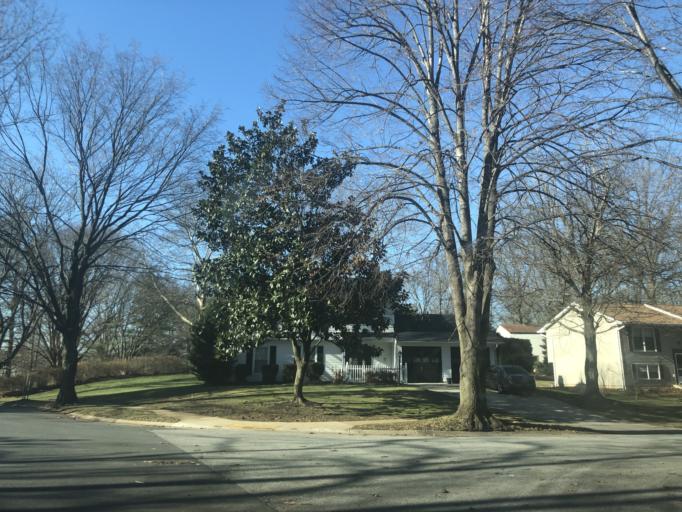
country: US
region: Maryland
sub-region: Howard County
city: Columbia
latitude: 39.1947
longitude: -76.8382
